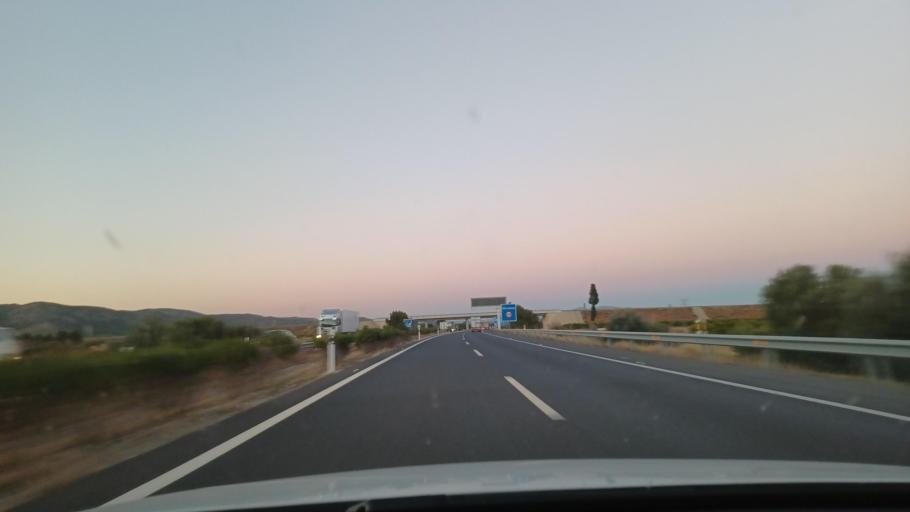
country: ES
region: Valencia
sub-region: Provincia de Castello
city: Orpesa/Oropesa del Mar
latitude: 40.1221
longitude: 0.1335
